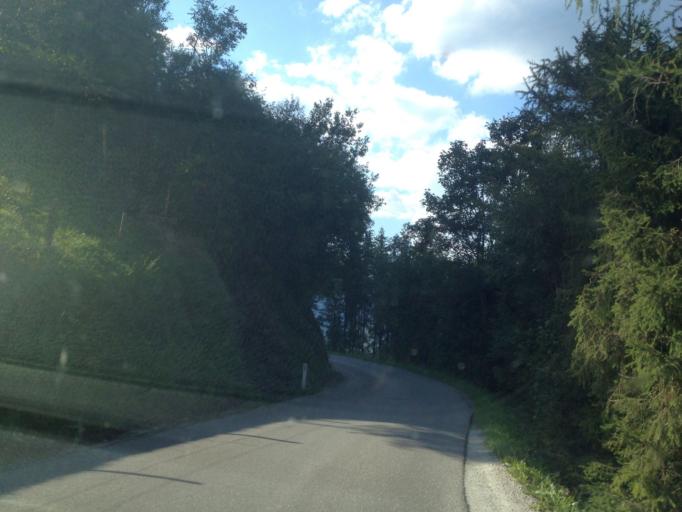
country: AT
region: Styria
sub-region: Politischer Bezirk Liezen
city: Schladming
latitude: 47.3792
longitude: 13.6144
